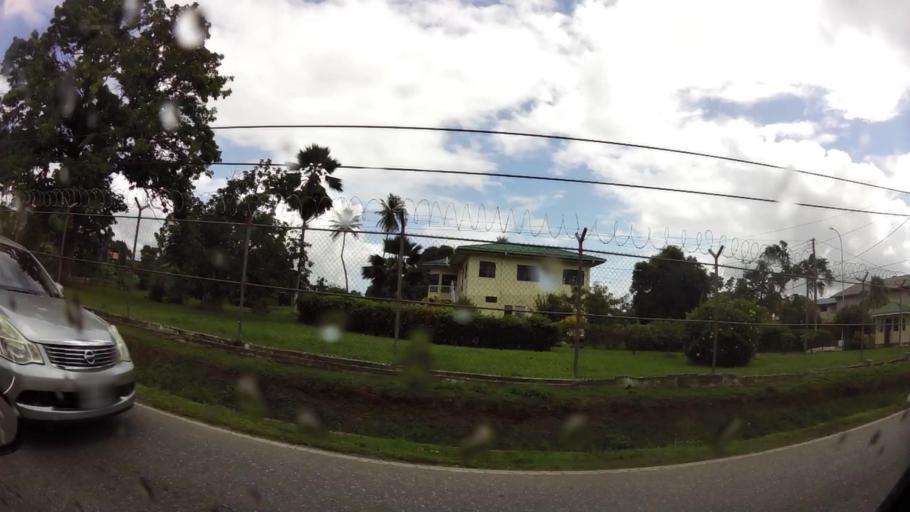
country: TT
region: Tunapuna/Piarco
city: Arouca
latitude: 10.6285
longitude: -61.3390
